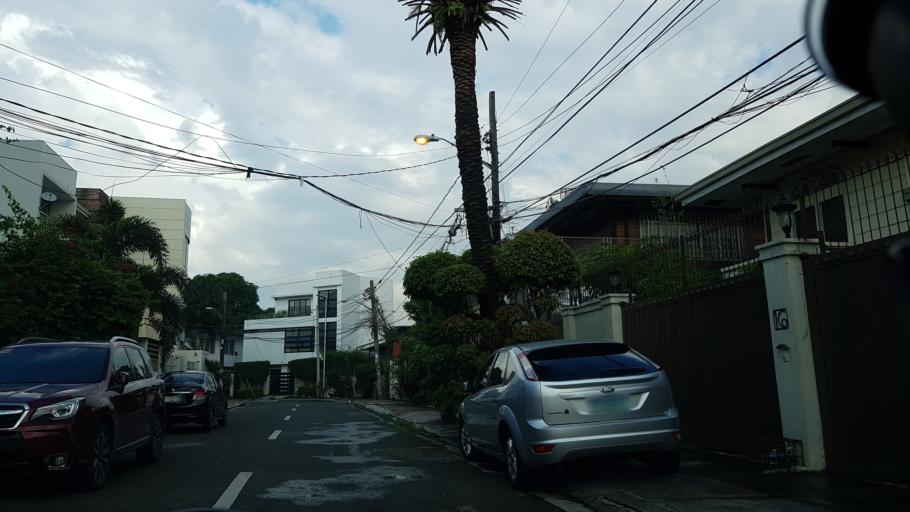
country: PH
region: Metro Manila
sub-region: Quezon City
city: Quezon City
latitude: 14.6381
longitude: 121.0591
